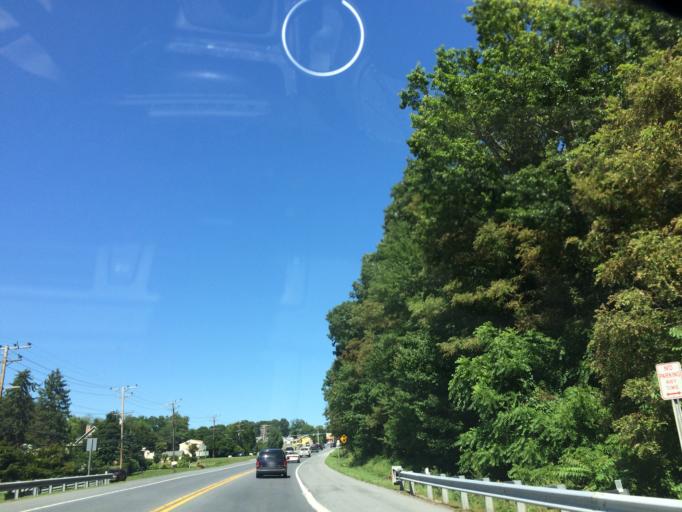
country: US
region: Maryland
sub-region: Carroll County
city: Eldersburg
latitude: 39.3976
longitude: -76.9558
